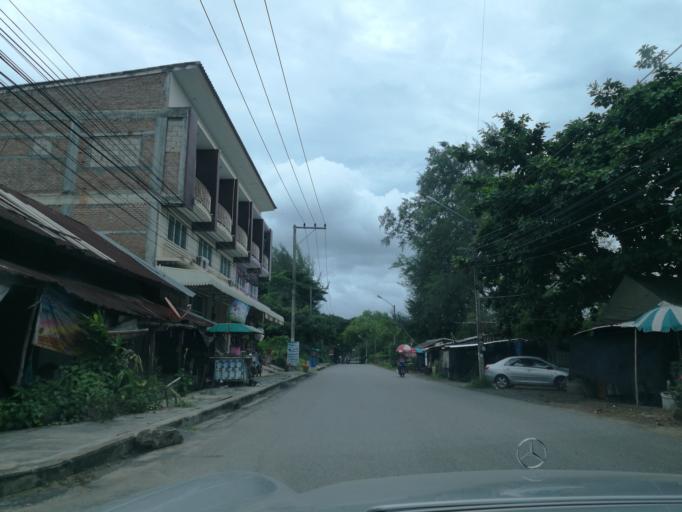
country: TH
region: Prachuap Khiri Khan
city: Prachuap Khiri Khan
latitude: 11.8106
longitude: 99.7931
